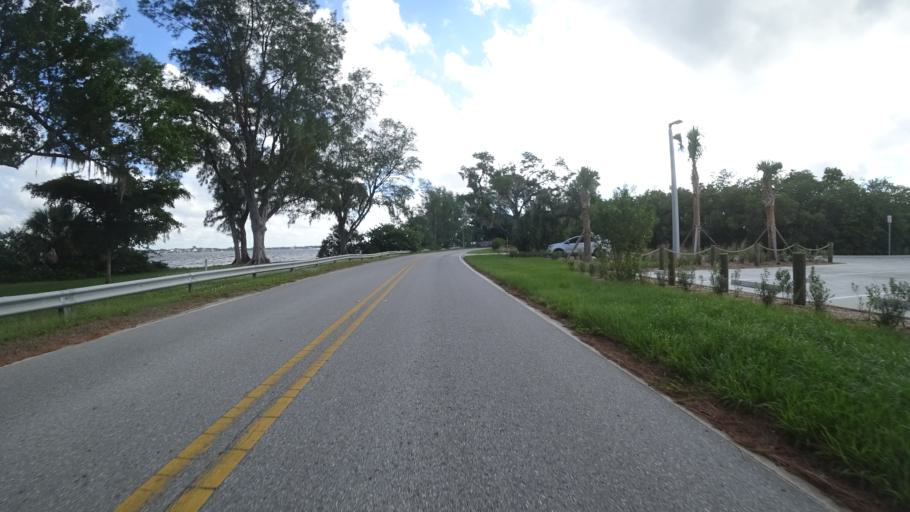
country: US
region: Florida
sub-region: Manatee County
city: West Bradenton
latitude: 27.5092
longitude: -82.6174
